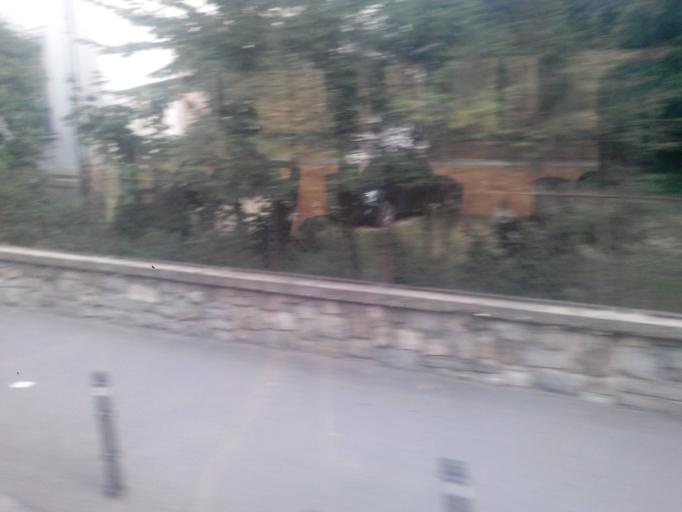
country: RO
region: Brasov
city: Brasov
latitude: 45.6463
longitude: 25.5948
